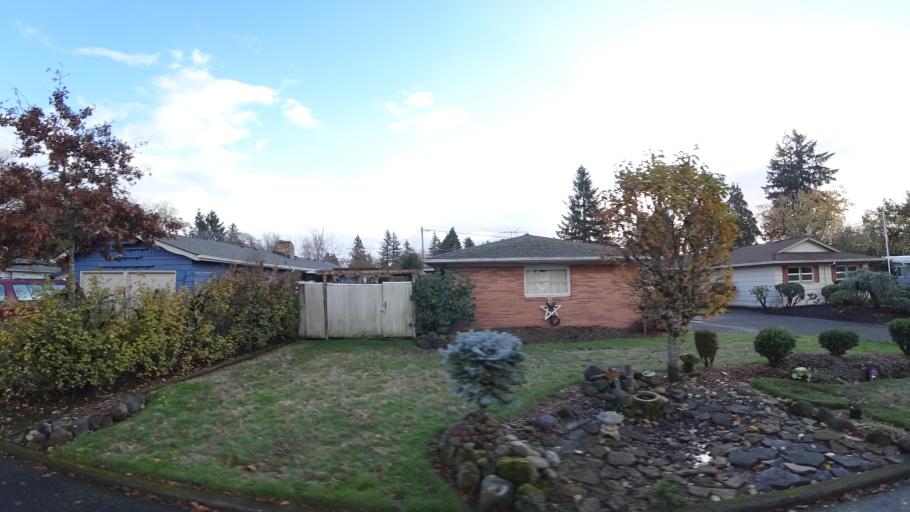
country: US
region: Oregon
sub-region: Multnomah County
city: Lents
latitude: 45.5210
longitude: -122.5498
